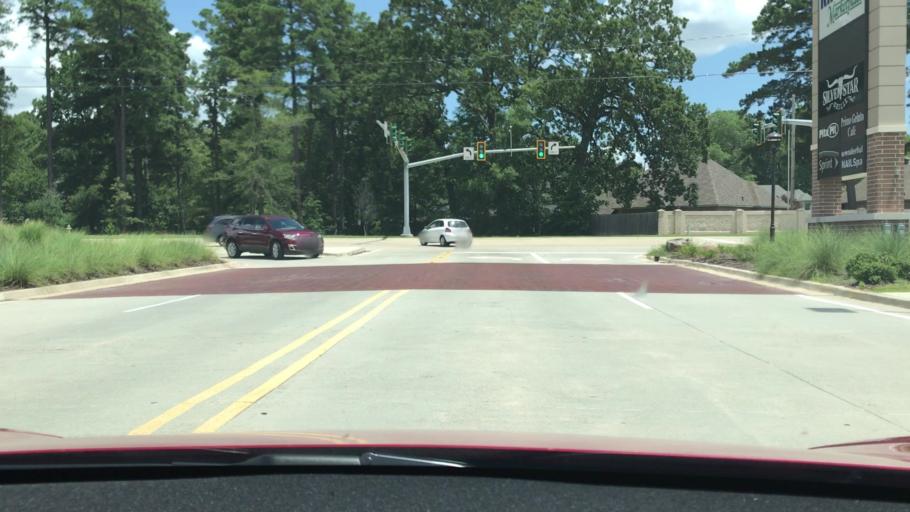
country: US
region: Louisiana
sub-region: Bossier Parish
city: Bossier City
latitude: 32.3963
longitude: -93.7290
